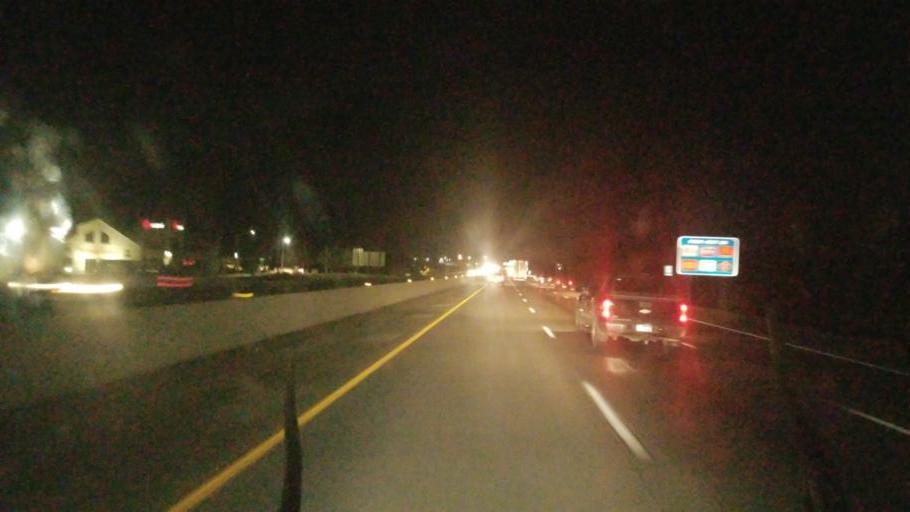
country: US
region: Missouri
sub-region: Jackson County
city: Blue Springs
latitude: 39.0320
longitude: -94.2876
